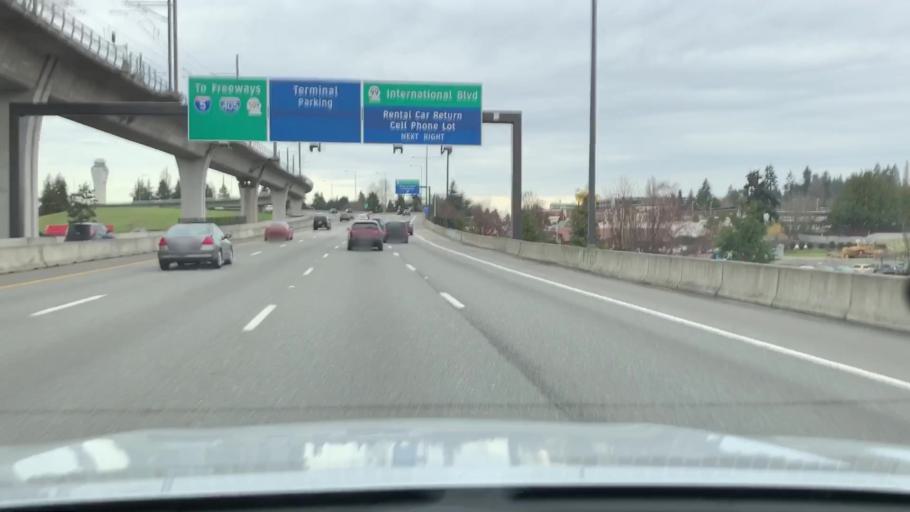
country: US
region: Washington
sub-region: King County
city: SeaTac
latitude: 47.4470
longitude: -122.2968
